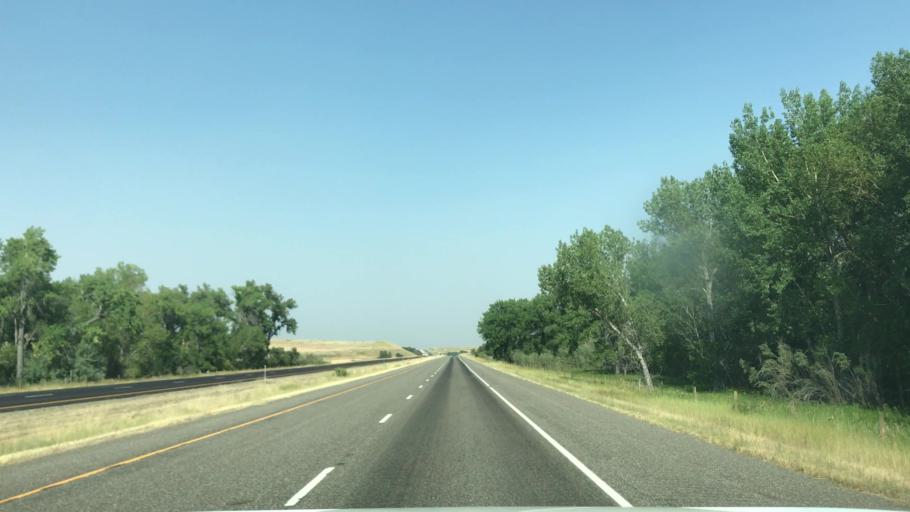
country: US
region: Montana
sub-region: Cascade County
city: Sun Prairie
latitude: 47.2356
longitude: -111.7433
